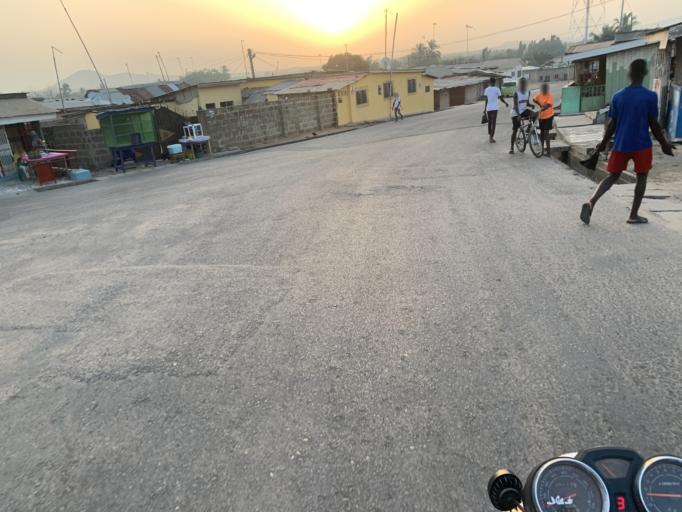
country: GH
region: Central
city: Winneba
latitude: 5.3492
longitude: -0.6275
